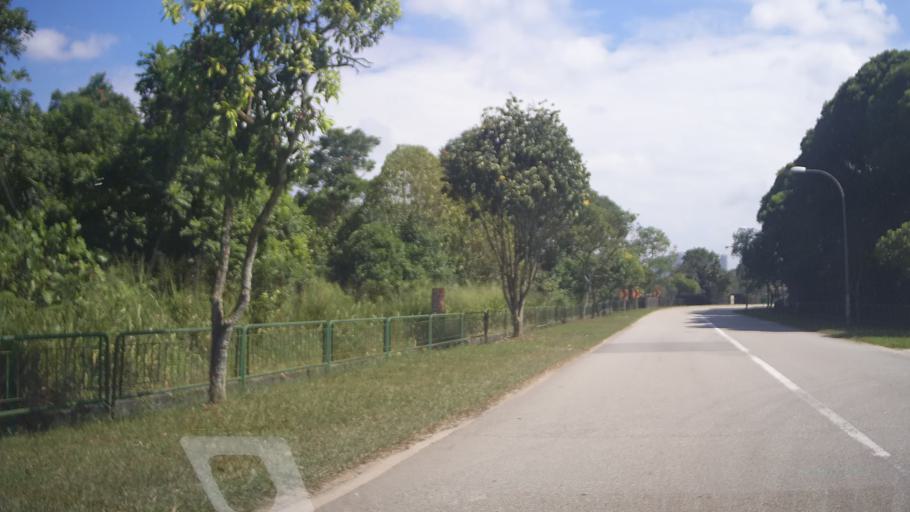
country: MY
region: Johor
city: Johor Bahru
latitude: 1.4295
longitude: 103.7097
